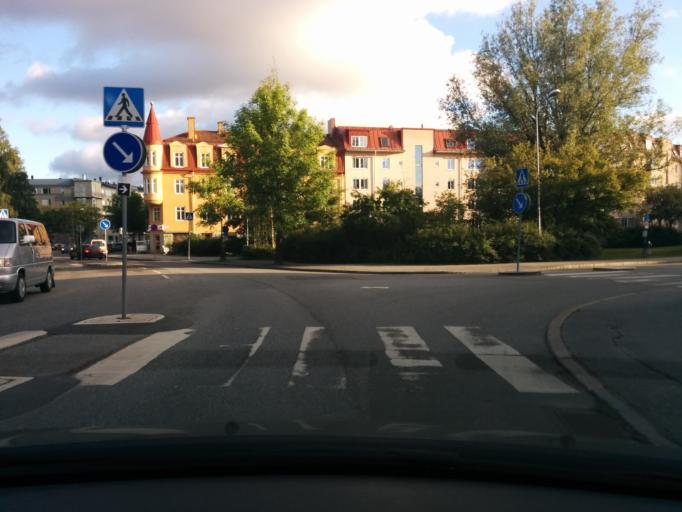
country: SE
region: Stockholm
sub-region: Stockholms Kommun
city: Arsta
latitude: 59.3011
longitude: 18.0042
